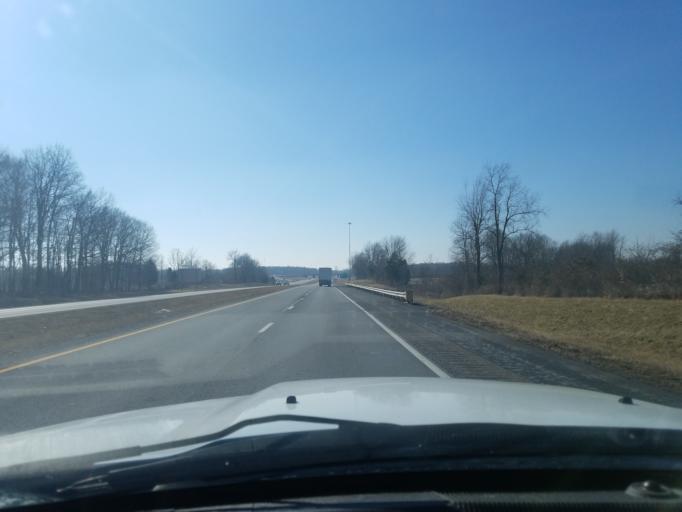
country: US
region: Kentucky
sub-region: Hardin County
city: Elizabethtown
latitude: 37.6618
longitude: -85.8834
